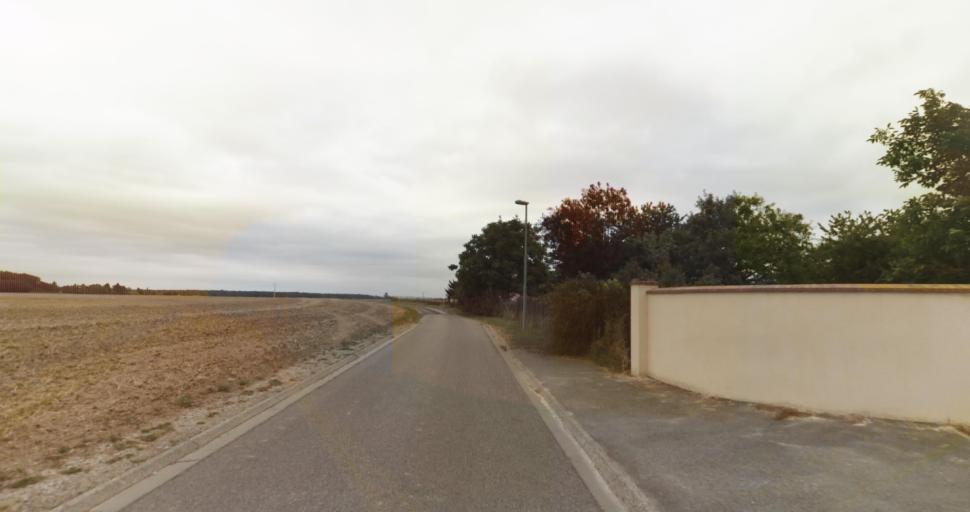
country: FR
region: Haute-Normandie
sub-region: Departement de l'Eure
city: La Couture-Boussey
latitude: 48.9078
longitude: 1.3945
